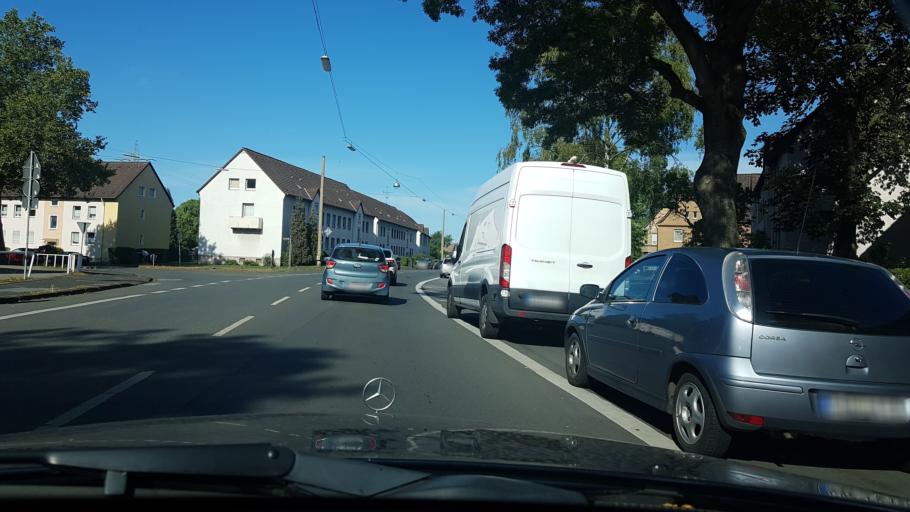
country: DE
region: North Rhine-Westphalia
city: Castrop-Rauxel
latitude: 51.5937
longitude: 7.3479
